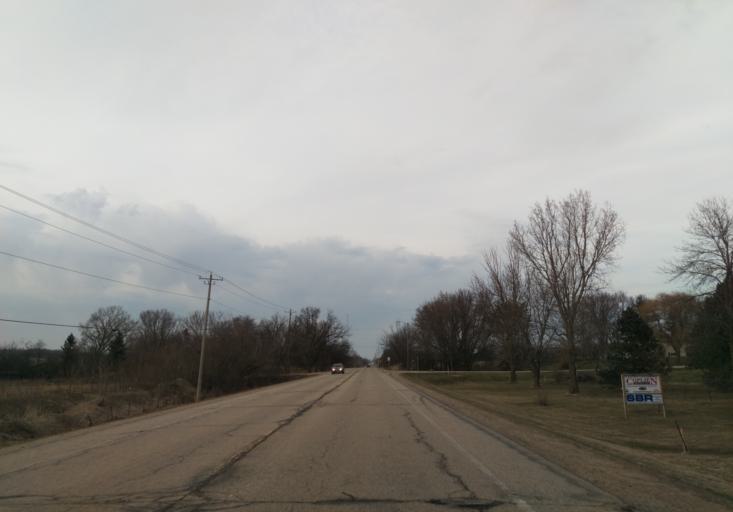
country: US
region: Wisconsin
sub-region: Dane County
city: Verona
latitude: 43.0108
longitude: -89.5336
